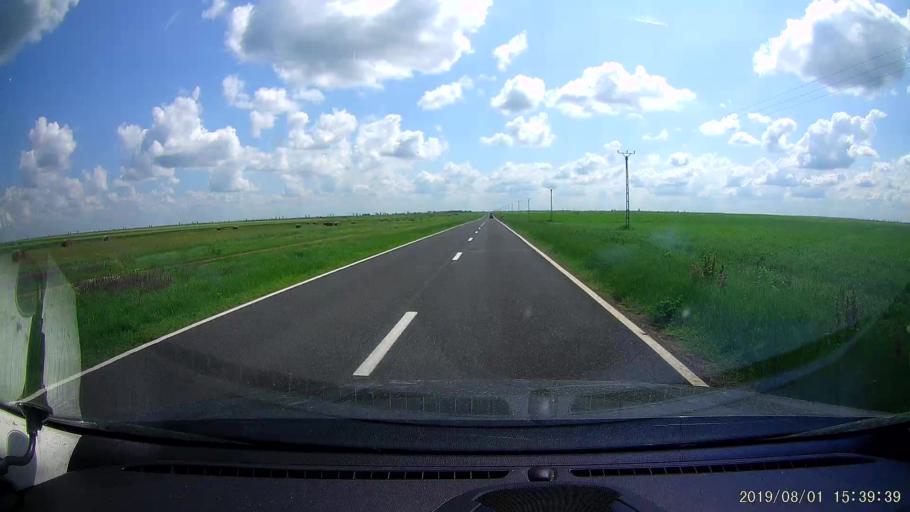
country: RO
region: Braila
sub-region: Comuna Baraganul
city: Baraganul
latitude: 44.8525
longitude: 27.5553
